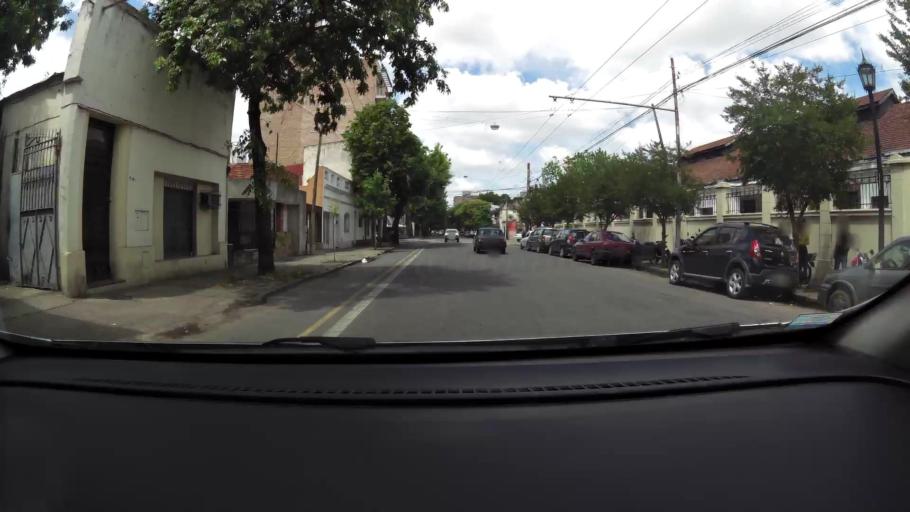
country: AR
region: Santa Fe
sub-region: Departamento de Rosario
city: Rosario
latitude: -32.9632
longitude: -60.6321
